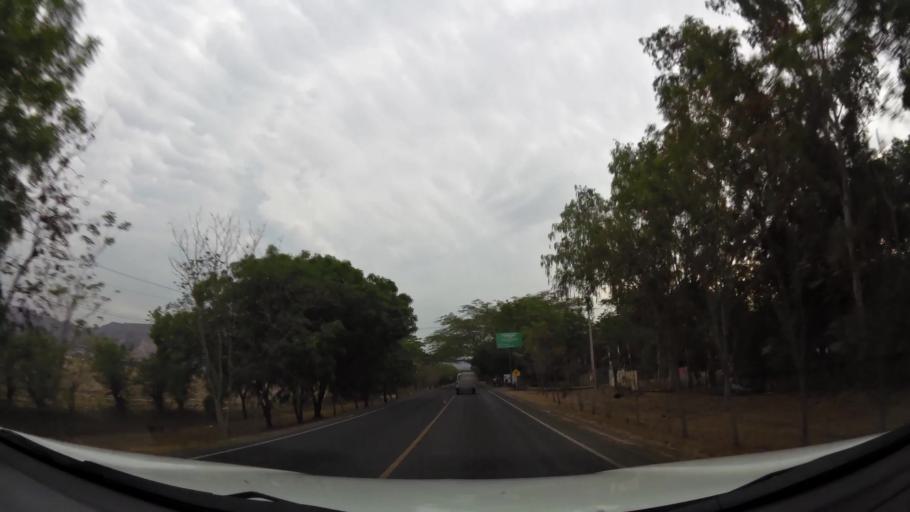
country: NI
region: Matagalpa
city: Ciudad Dario
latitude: 12.9098
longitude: -86.1760
